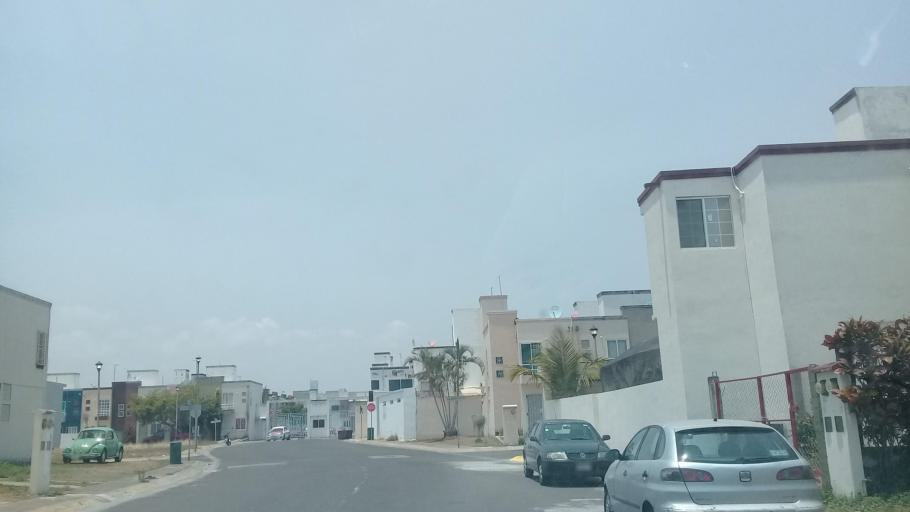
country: MX
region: Veracruz
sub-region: Veracruz
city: Hacienda Sotavento
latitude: 19.1333
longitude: -96.1750
